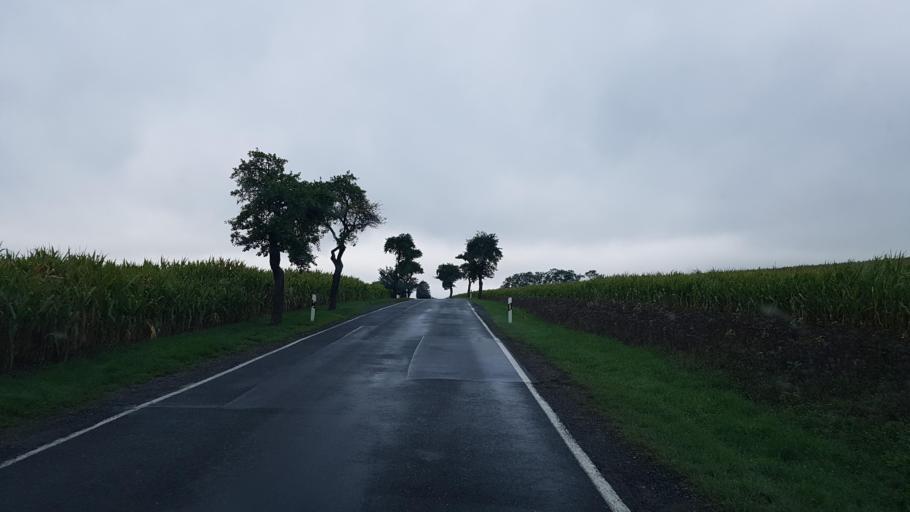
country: DE
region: Thuringia
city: Wurzbach
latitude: 50.5205
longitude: 11.5451
